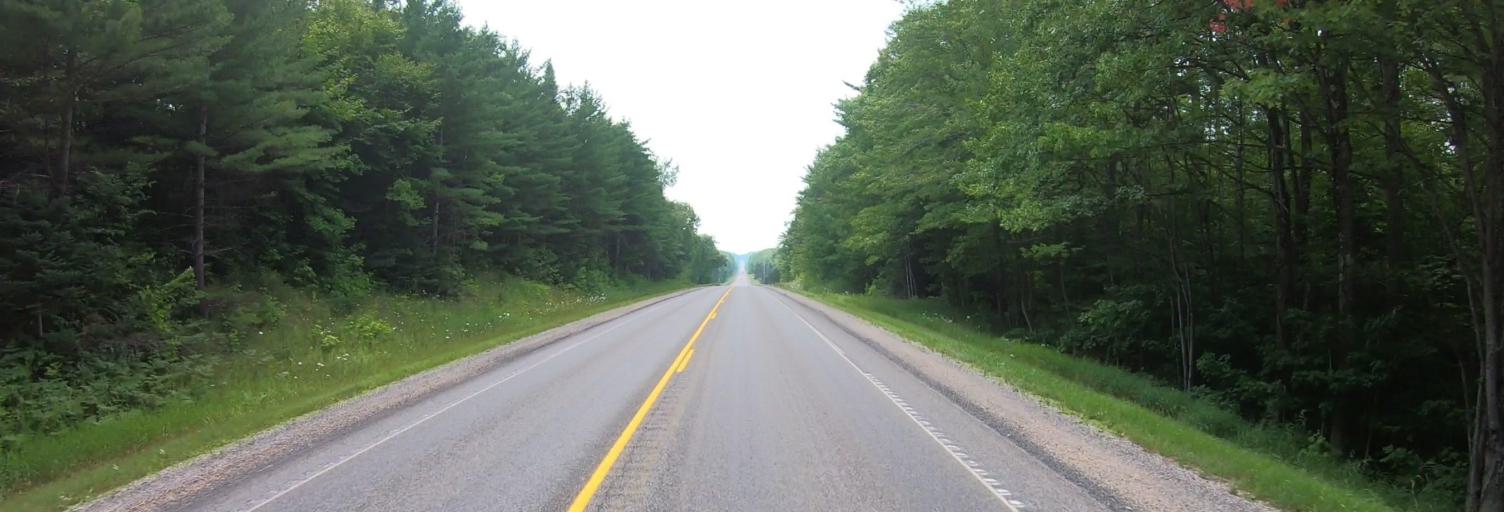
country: US
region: Michigan
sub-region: Alger County
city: Munising
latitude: 46.3744
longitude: -86.7025
